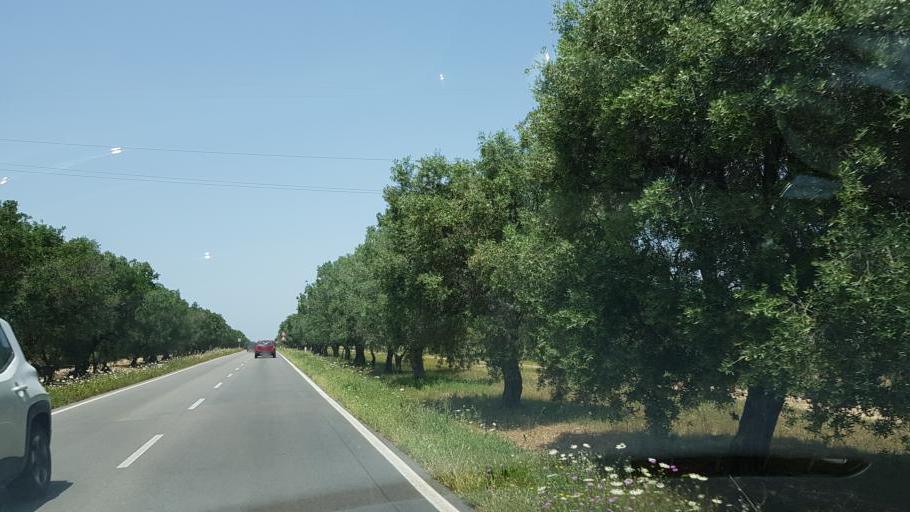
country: IT
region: Apulia
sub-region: Provincia di Brindisi
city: San Pancrazio Salentino
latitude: 40.3598
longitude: 17.8429
